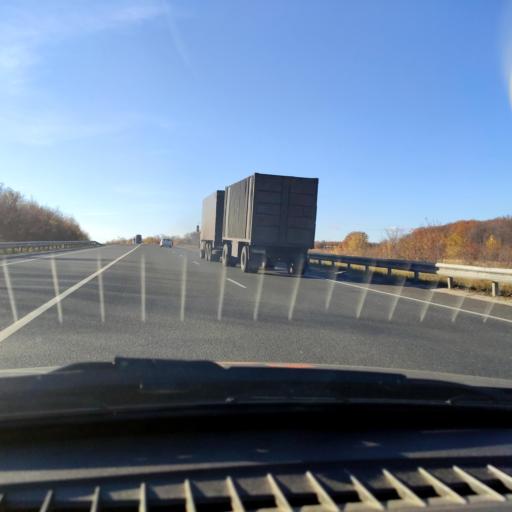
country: RU
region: Samara
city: Mezhdurechensk
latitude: 53.2591
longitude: 49.0897
